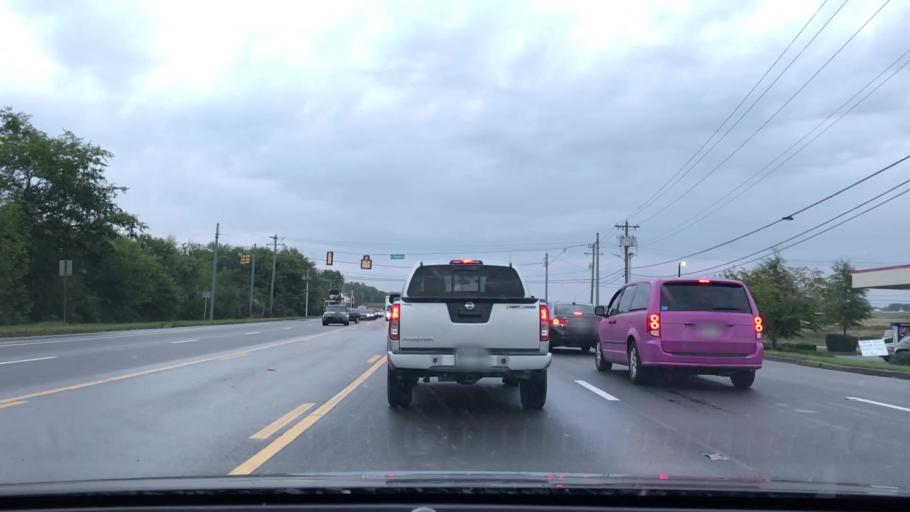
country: US
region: Tennessee
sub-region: Sumner County
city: Gallatin
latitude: 36.3869
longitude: -86.4805
